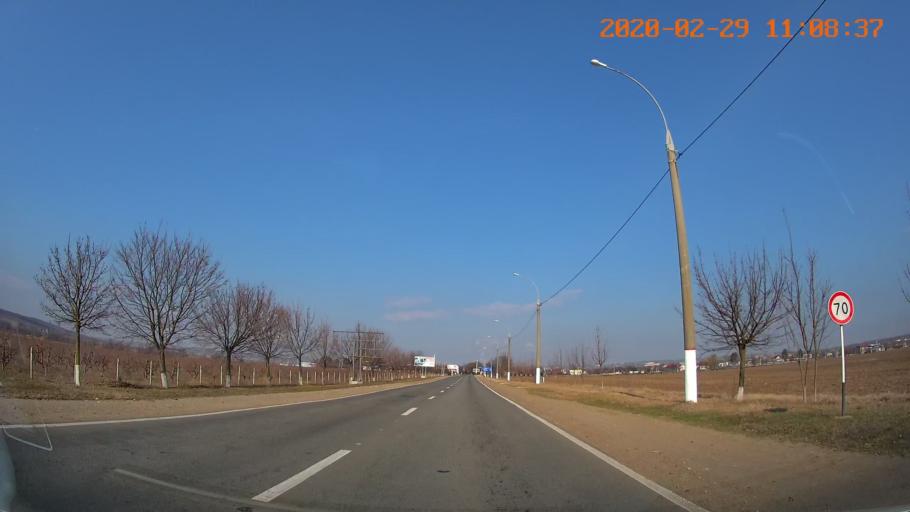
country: MD
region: Criuleni
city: Criuleni
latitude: 47.2355
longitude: 29.1743
